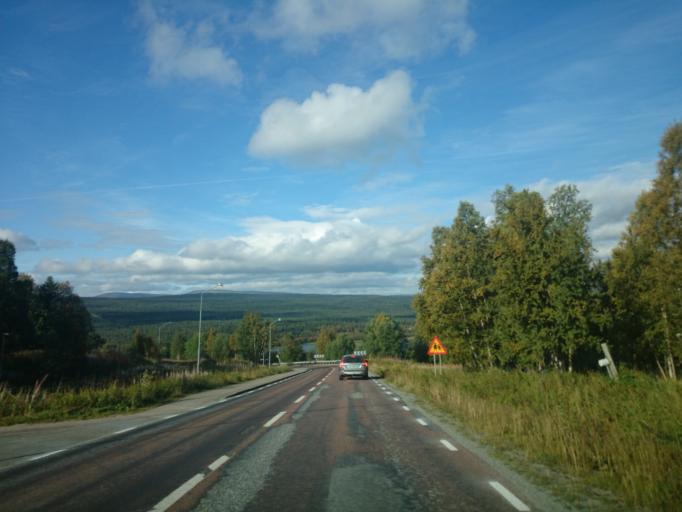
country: NO
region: Hedmark
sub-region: Engerdal
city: Engerdal
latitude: 62.5455
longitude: 12.5512
